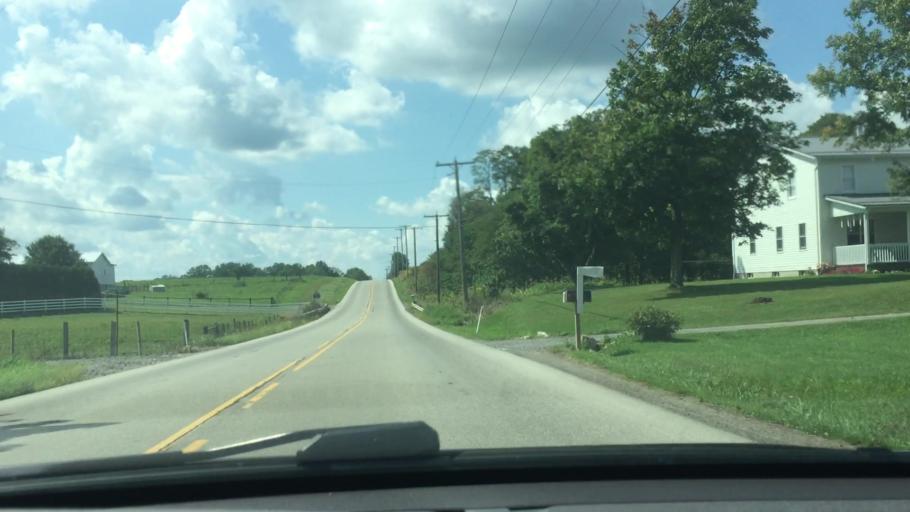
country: US
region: Pennsylvania
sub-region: Lawrence County
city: New Wilmington
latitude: 41.1204
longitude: -80.3890
